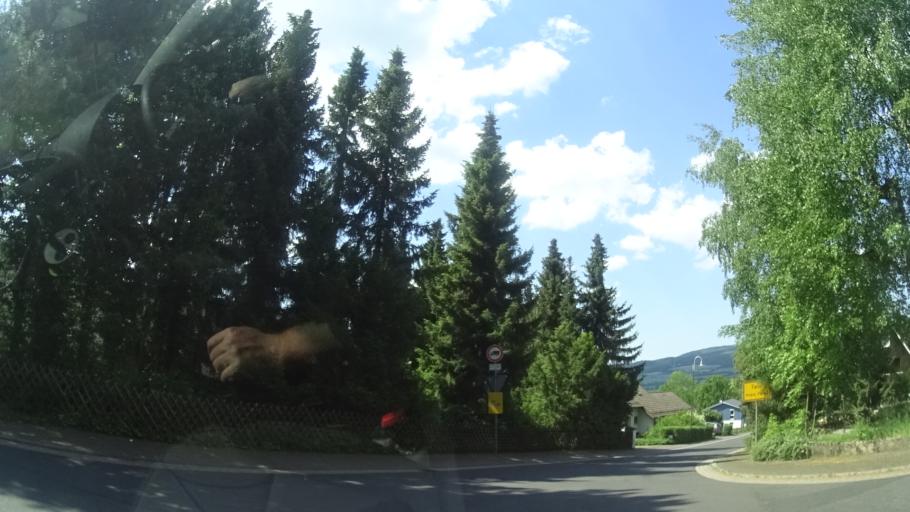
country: DE
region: Hesse
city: Tann
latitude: 50.6394
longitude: 10.0283
